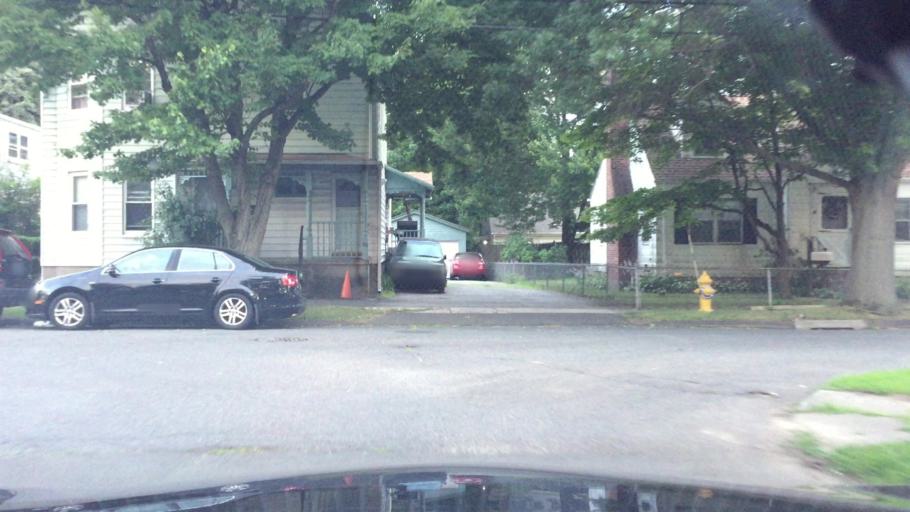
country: US
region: Connecticut
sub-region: Fairfield County
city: Stratford
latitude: 41.1912
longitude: -73.1250
